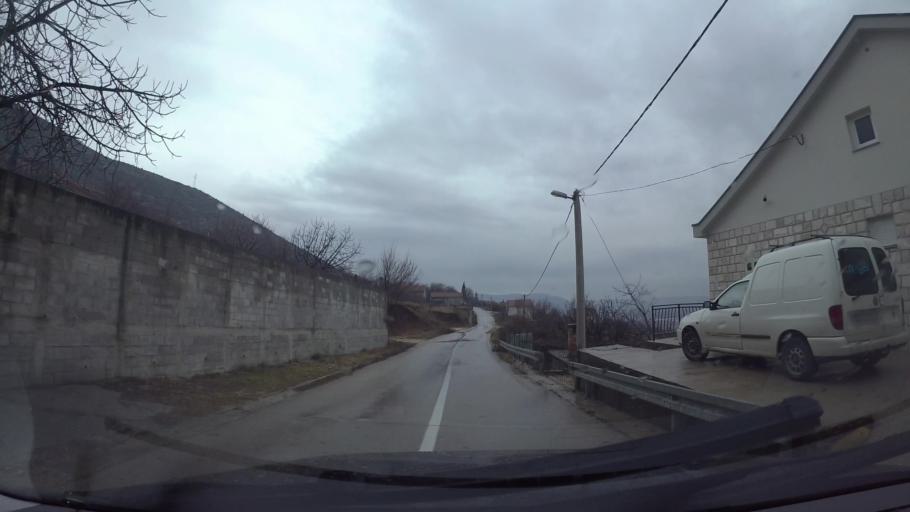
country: BA
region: Federation of Bosnia and Herzegovina
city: Rodoc
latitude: 43.3017
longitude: 17.8539
